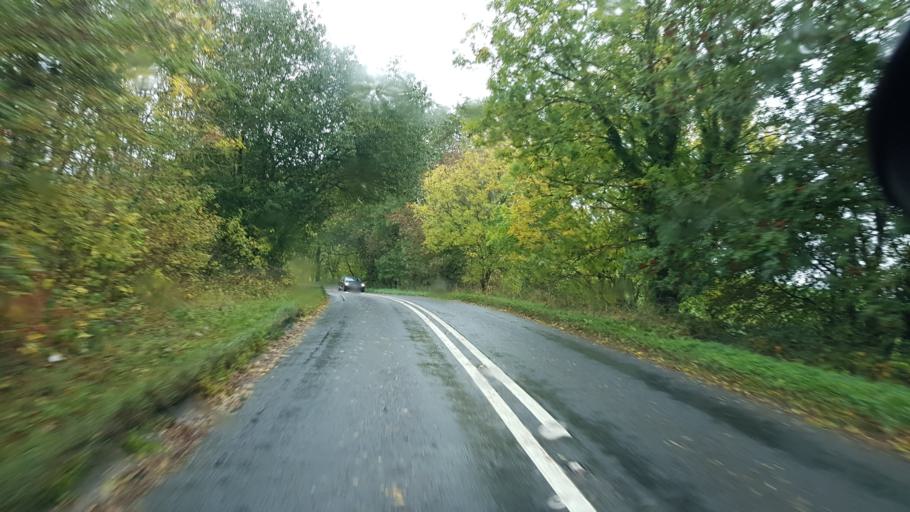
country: GB
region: England
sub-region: Gloucestershire
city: Stow on the Wold
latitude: 51.9421
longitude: -1.7497
